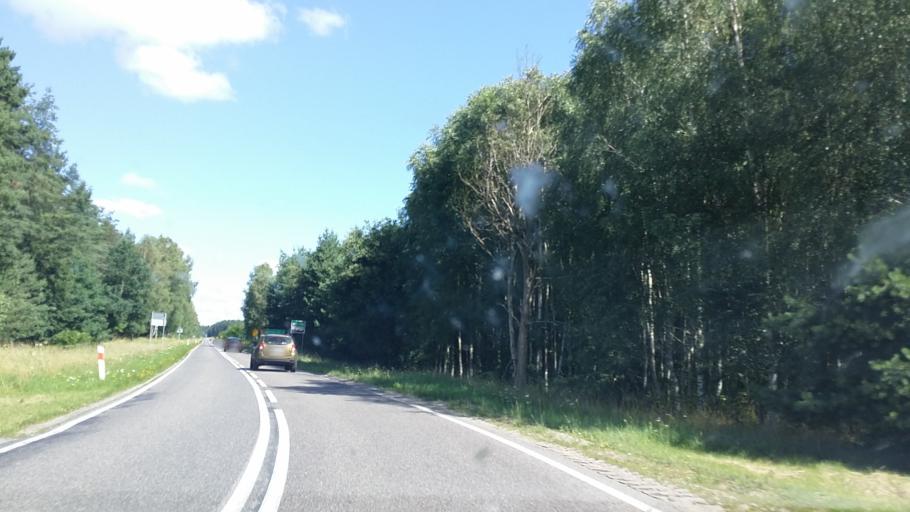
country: PL
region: West Pomeranian Voivodeship
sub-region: Powiat drawski
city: Drawsko Pomorskie
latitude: 53.4444
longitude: 15.8304
